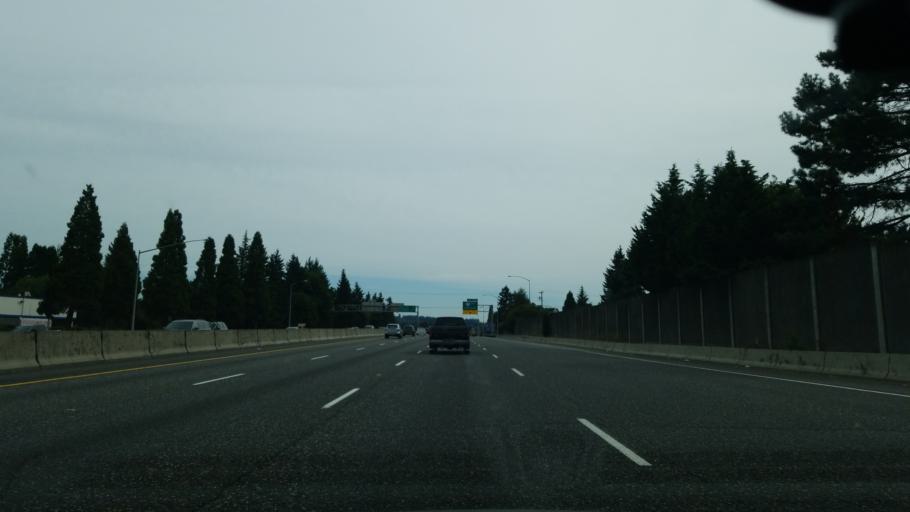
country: US
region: Oregon
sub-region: Clackamas County
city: Clackamas
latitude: 45.4151
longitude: -122.5741
